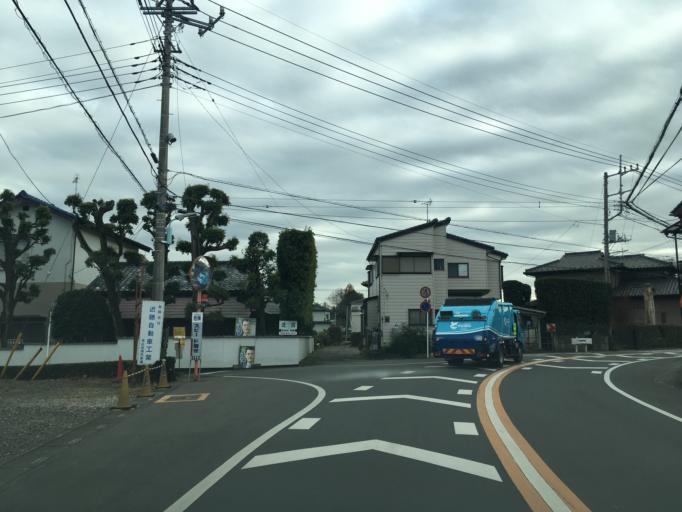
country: JP
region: Saitama
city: Sayama
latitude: 35.7927
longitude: 139.4010
